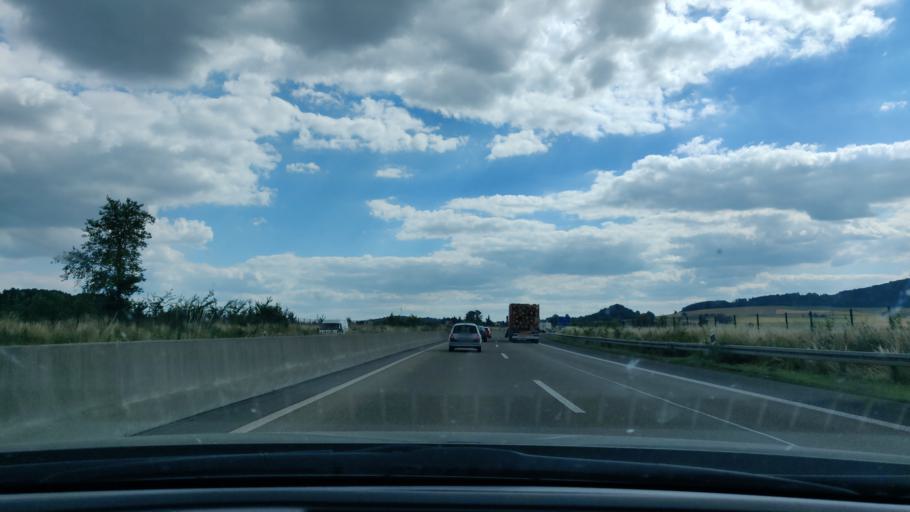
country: DE
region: Hesse
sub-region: Regierungsbezirk Kassel
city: Baunatal
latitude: 51.2044
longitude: 9.4101
